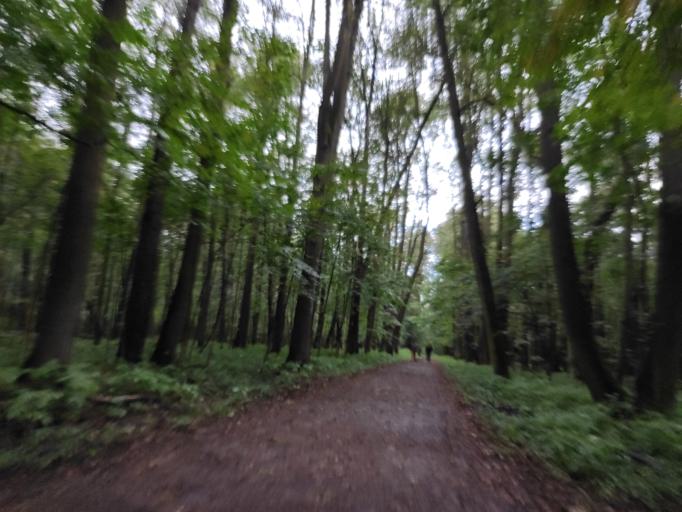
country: RU
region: Moskovskaya
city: Izmaylovo
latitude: 55.7761
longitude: 37.7889
